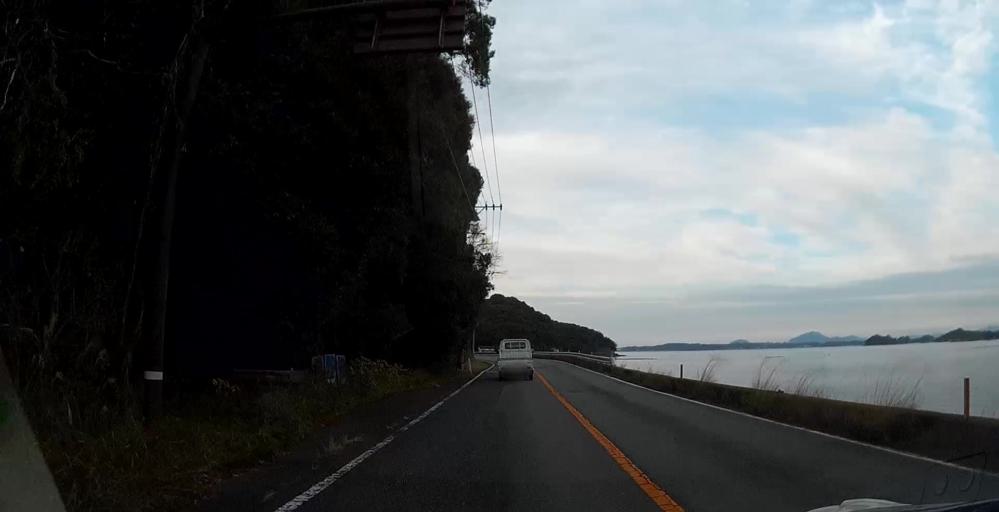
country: JP
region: Kumamoto
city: Hondo
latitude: 32.5021
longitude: 130.3905
